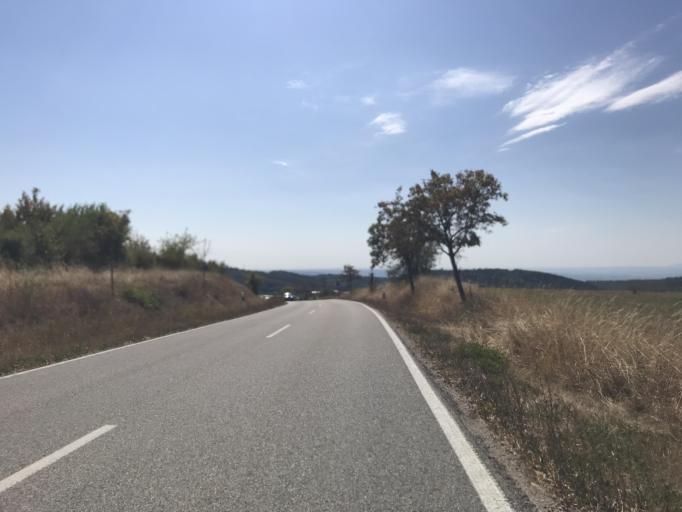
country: DE
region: Hesse
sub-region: Regierungsbezirk Darmstadt
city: Rudesheim am Rhein
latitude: 50.0399
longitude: 7.9386
